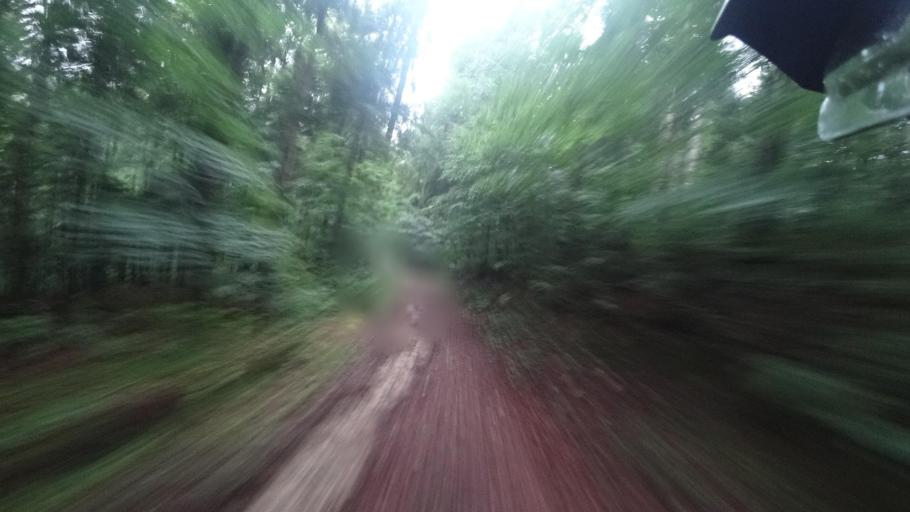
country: HR
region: Licko-Senjska
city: Jezerce
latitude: 44.8212
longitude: 15.6155
